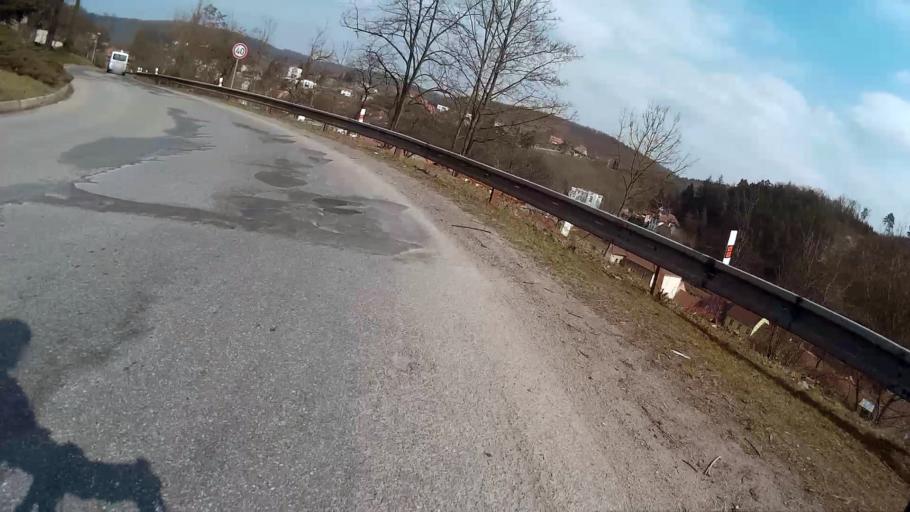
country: CZ
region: South Moravian
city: Bilovice nad Svitavou
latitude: 49.2443
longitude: 16.6721
